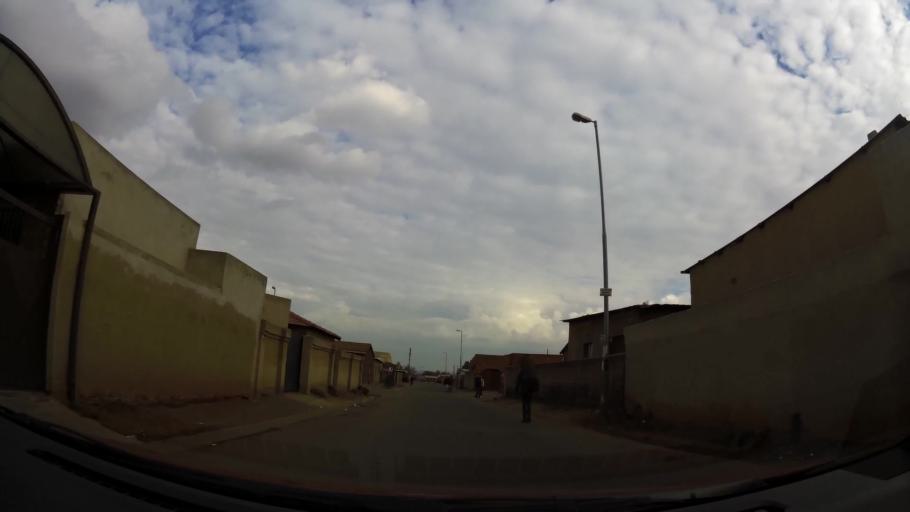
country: ZA
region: Gauteng
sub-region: City of Johannesburg Metropolitan Municipality
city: Soweto
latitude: -26.2473
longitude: 27.8343
